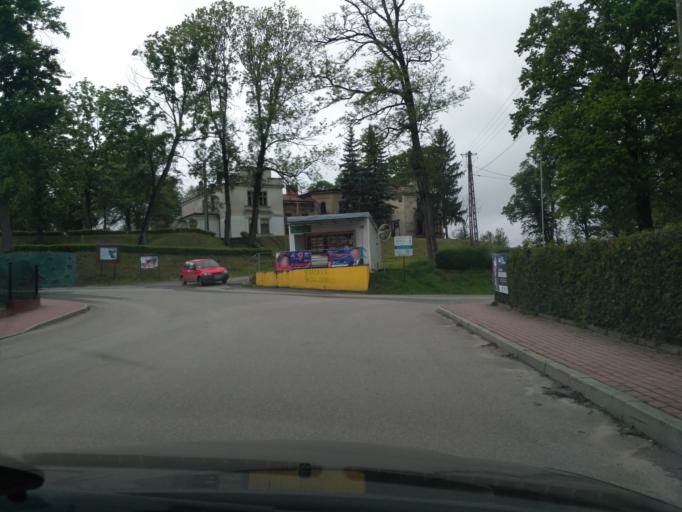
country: PL
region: Subcarpathian Voivodeship
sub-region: Powiat jasielski
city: Brzyska
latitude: 49.8206
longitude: 21.3912
